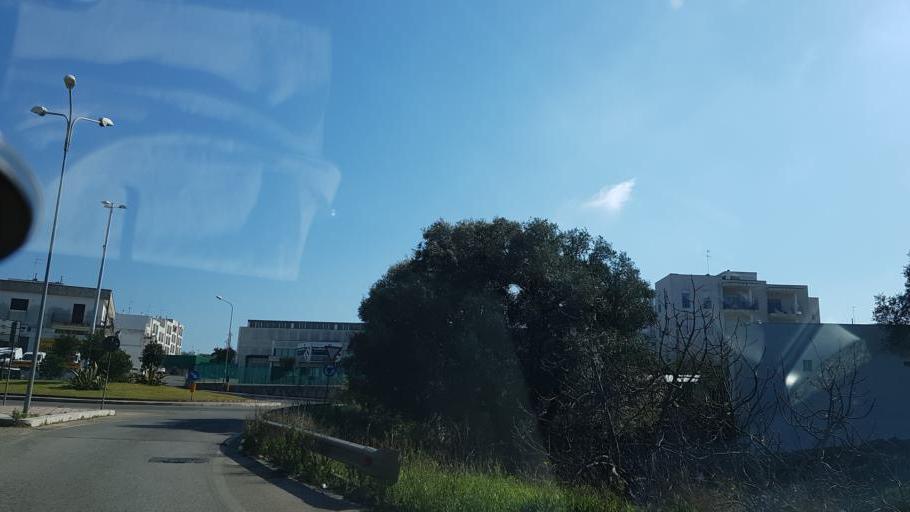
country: IT
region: Apulia
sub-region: Provincia di Brindisi
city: Ostuni
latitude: 40.7248
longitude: 17.5914
